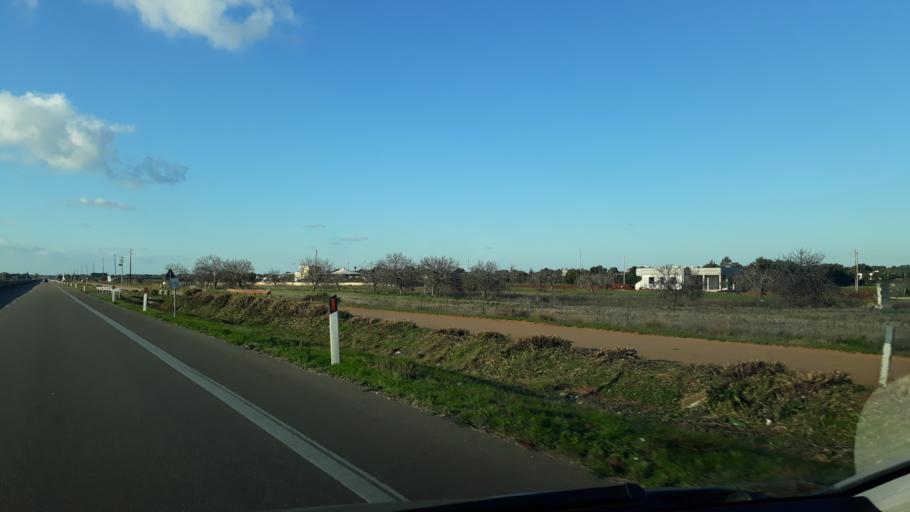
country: IT
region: Apulia
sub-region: Provincia di Brindisi
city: San Vito dei Normanni
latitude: 40.7303
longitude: 17.7349
